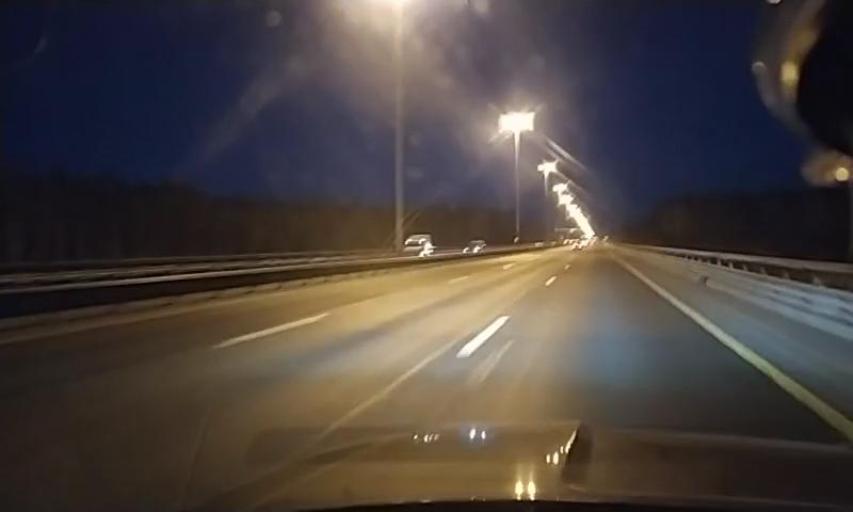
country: RU
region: St.-Petersburg
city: Pesochnyy
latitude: 60.0916
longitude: 30.0979
